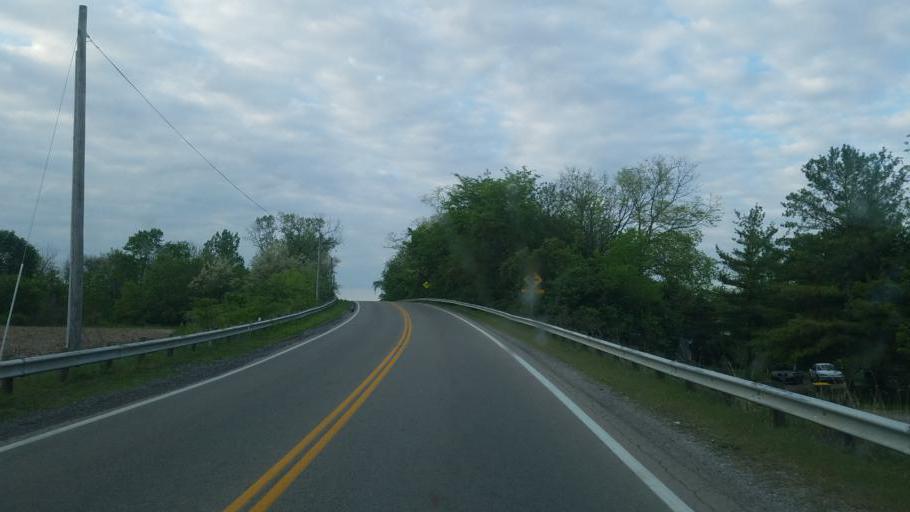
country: US
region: Ohio
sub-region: Madison County
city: Mount Sterling
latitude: 39.7431
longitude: -83.2416
